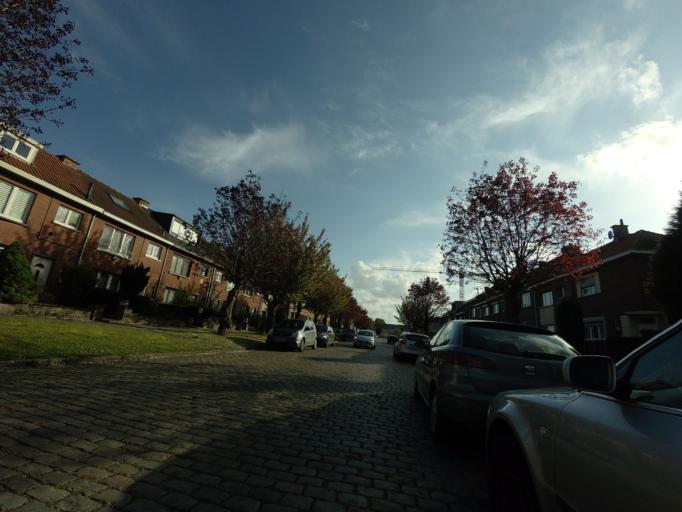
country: BE
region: Flanders
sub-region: Provincie Vlaams-Brabant
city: Grimbergen
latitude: 50.9127
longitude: 4.3759
